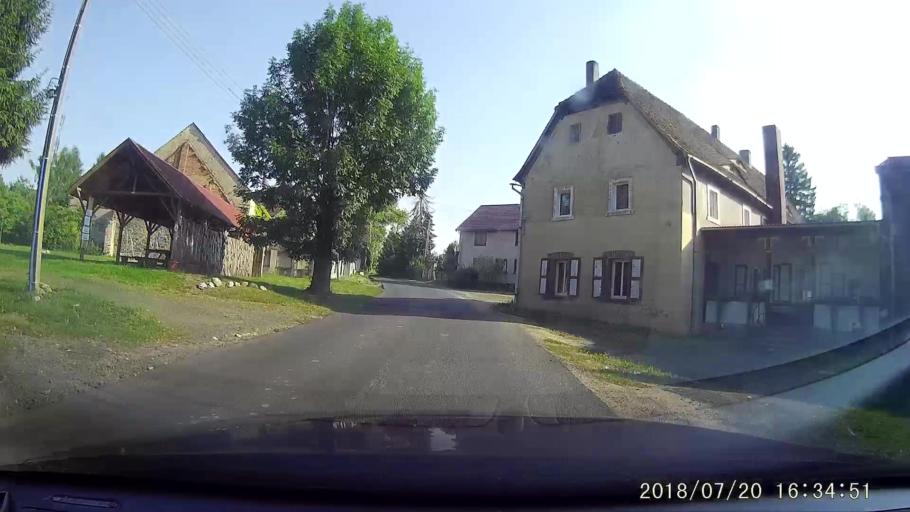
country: PL
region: Lower Silesian Voivodeship
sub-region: Powiat zgorzelecki
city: Sulikow
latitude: 51.0818
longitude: 15.1018
